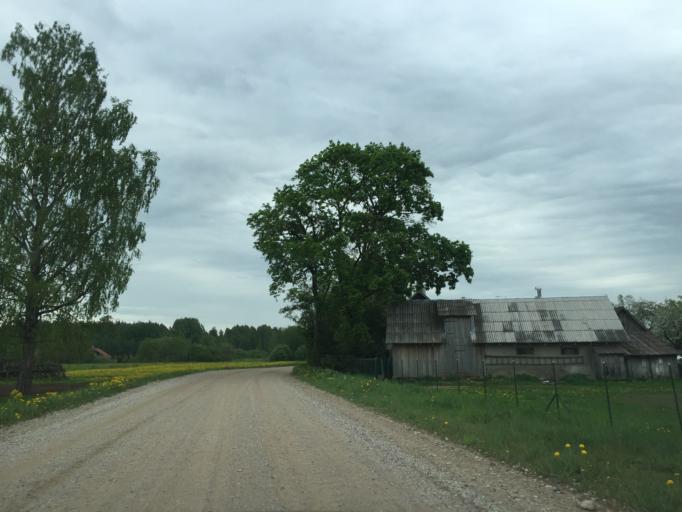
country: LV
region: Lielvarde
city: Lielvarde
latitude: 56.8063
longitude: 24.8373
